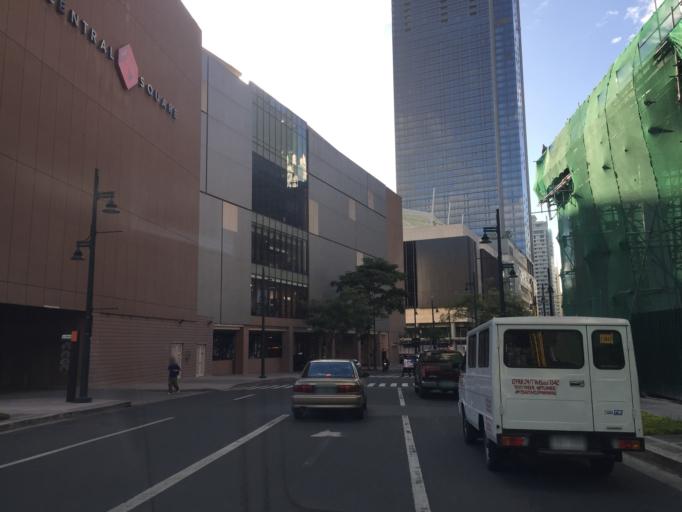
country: PH
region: Metro Manila
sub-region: Makati City
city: Makati City
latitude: 14.5524
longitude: 121.0492
